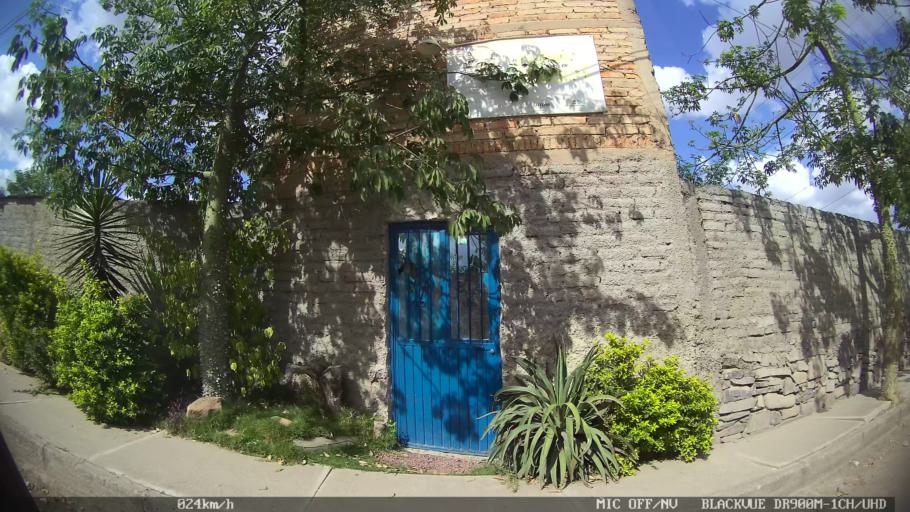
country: MX
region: Jalisco
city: Tlaquepaque
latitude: 20.6649
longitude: -103.2643
